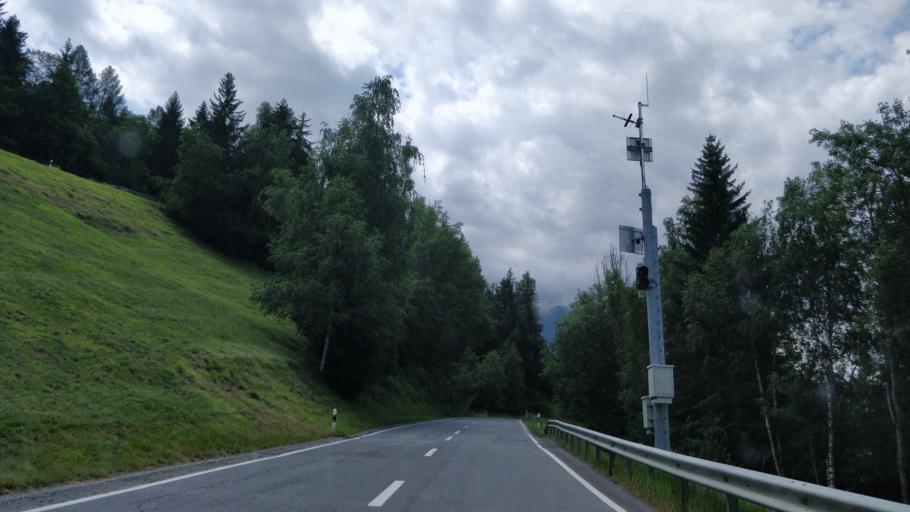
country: CH
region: Grisons
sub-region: Surselva District
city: Ilanz
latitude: 46.7090
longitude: 9.1936
